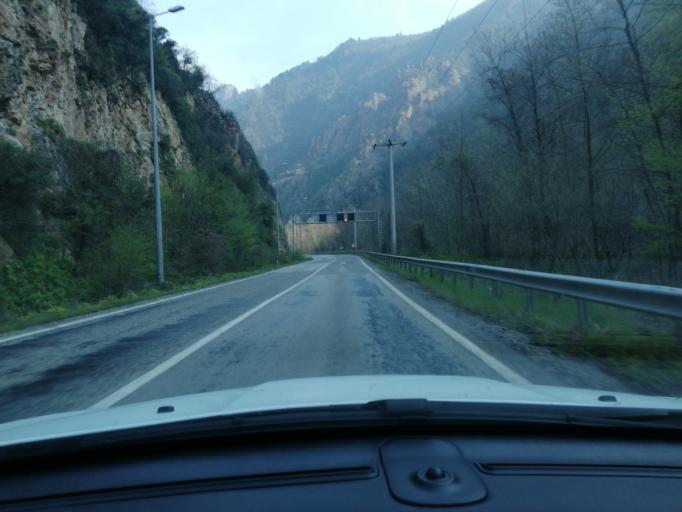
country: TR
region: Karabuk
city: Yenice
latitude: 41.1780
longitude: 32.4474
